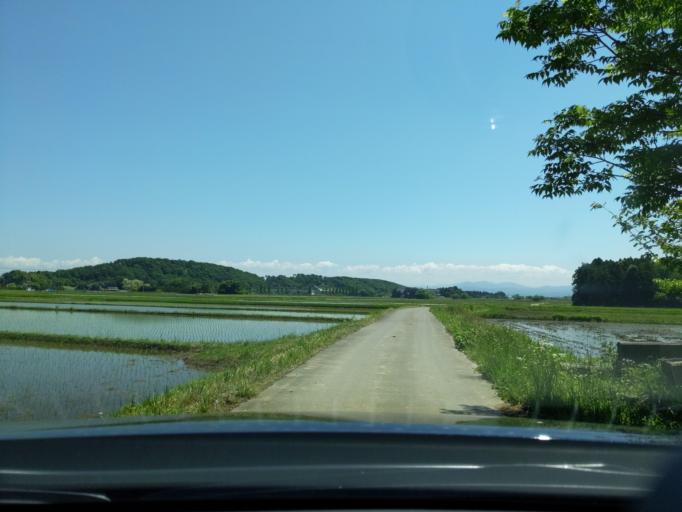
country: JP
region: Fukushima
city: Koriyama
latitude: 37.3942
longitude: 140.2901
